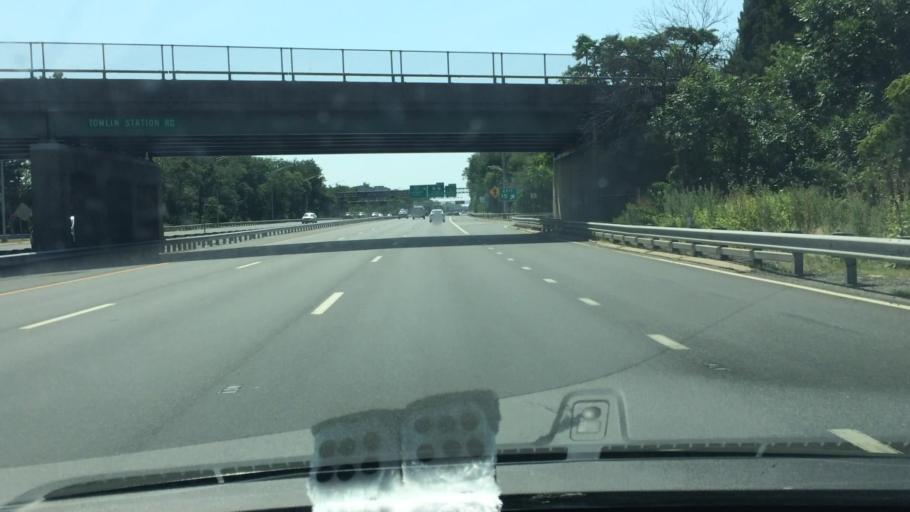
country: US
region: New Jersey
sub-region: Gloucester County
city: Gibbstown
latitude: 39.8079
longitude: -75.2896
